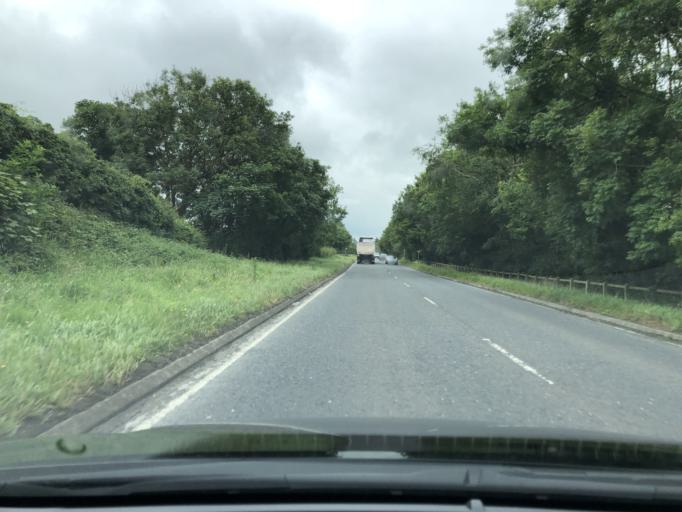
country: GB
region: Northern Ireland
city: Ballynahinch
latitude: 54.3429
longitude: -5.8439
